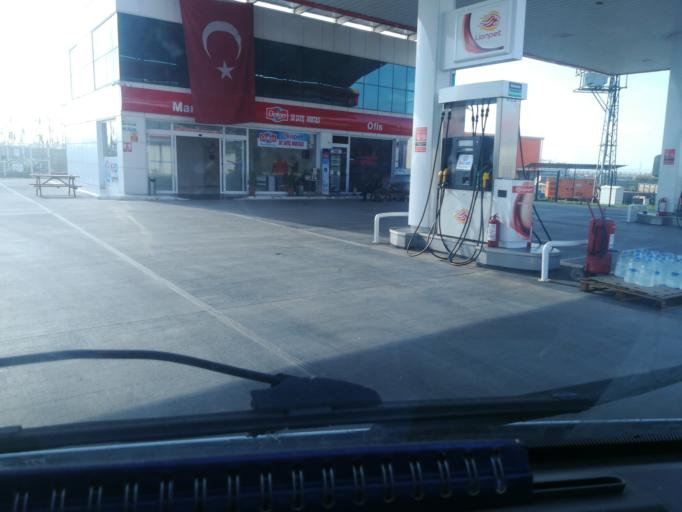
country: TR
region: Adana
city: Ceyhan
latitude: 37.0521
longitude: 35.7776
